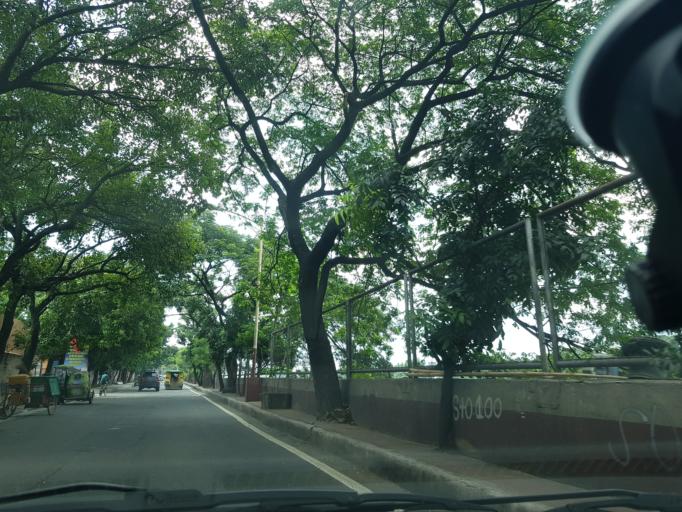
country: PH
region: Metro Manila
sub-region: Pasig
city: Pasig City
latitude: 14.5909
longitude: 121.0920
